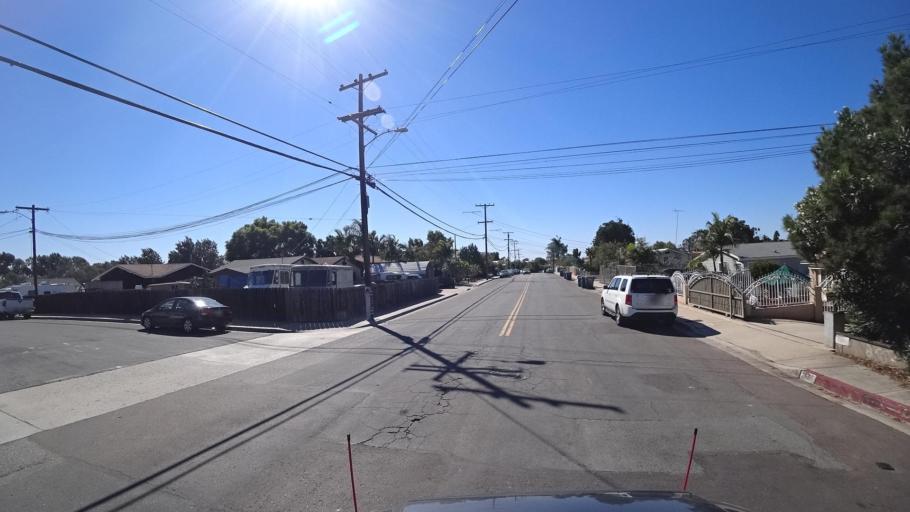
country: US
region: California
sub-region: San Diego County
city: National City
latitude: 32.6675
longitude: -117.0737
